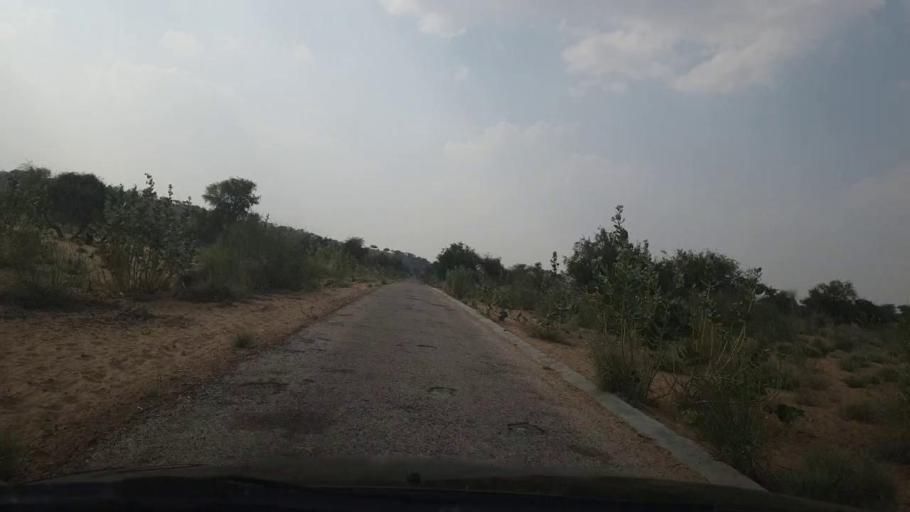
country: PK
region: Sindh
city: Islamkot
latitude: 24.9640
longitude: 70.6099
